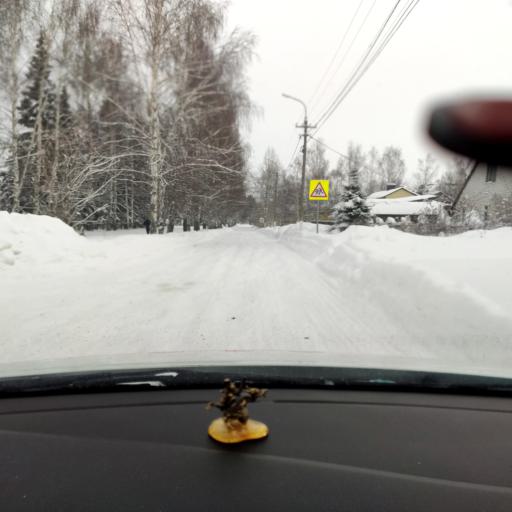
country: RU
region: Tatarstan
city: Stolbishchi
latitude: 55.6102
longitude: 49.1416
